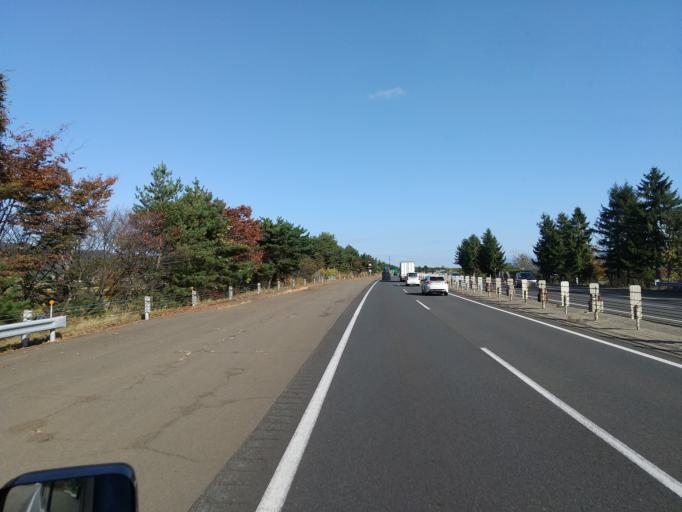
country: JP
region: Iwate
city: Morioka-shi
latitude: 39.5928
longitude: 141.1177
